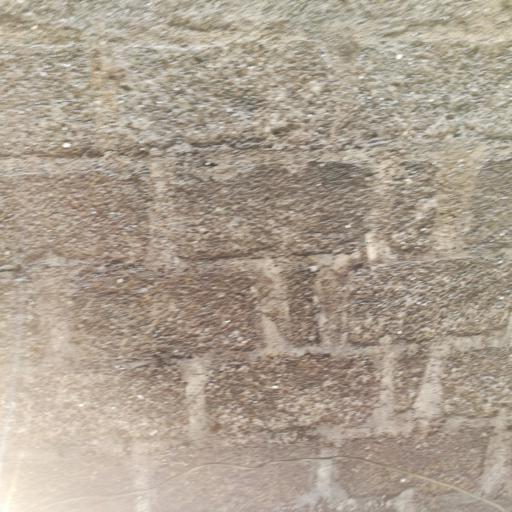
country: NG
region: Rivers
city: Port Harcourt
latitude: 4.8423
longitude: 7.0722
